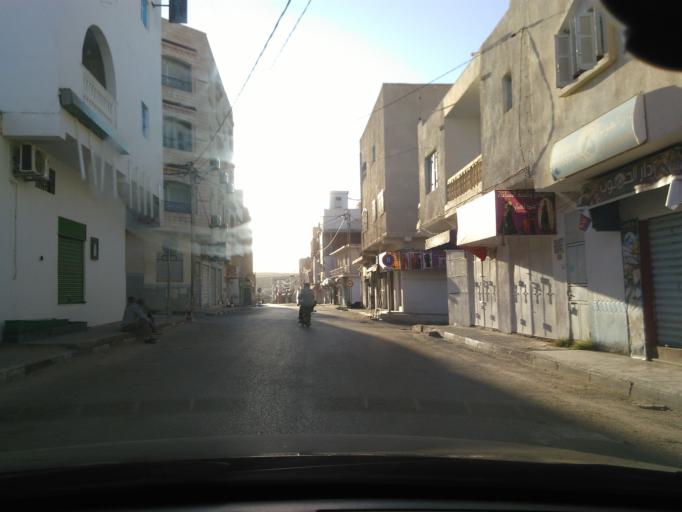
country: TN
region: Tataouine
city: Tataouine
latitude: 32.9270
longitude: 10.4504
